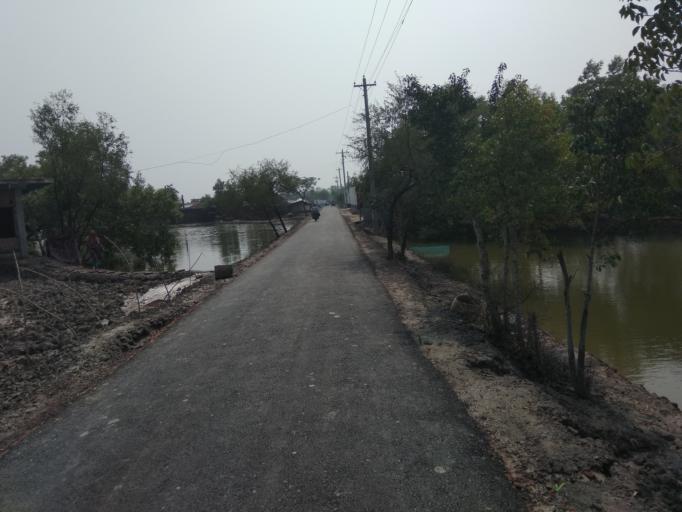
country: IN
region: West Bengal
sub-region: North 24 Parganas
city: Gosaba
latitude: 22.2626
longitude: 89.2224
